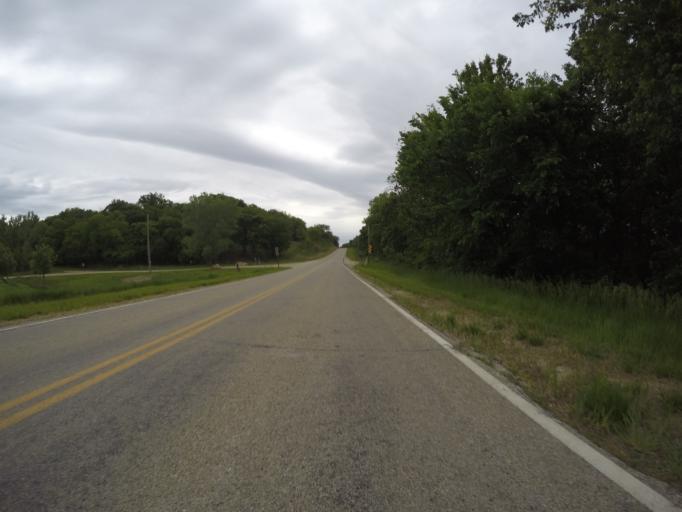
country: US
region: Kansas
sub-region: Pottawatomie County
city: Wamego
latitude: 39.1831
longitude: -96.3583
